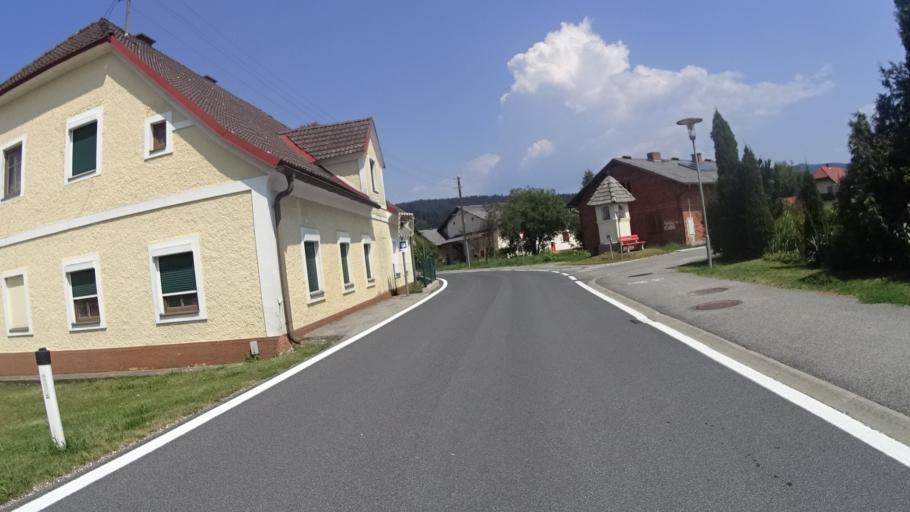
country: AT
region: Carinthia
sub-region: Politischer Bezirk Volkermarkt
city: Feistritz ob Bleiburg
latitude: 46.5741
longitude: 14.7710
